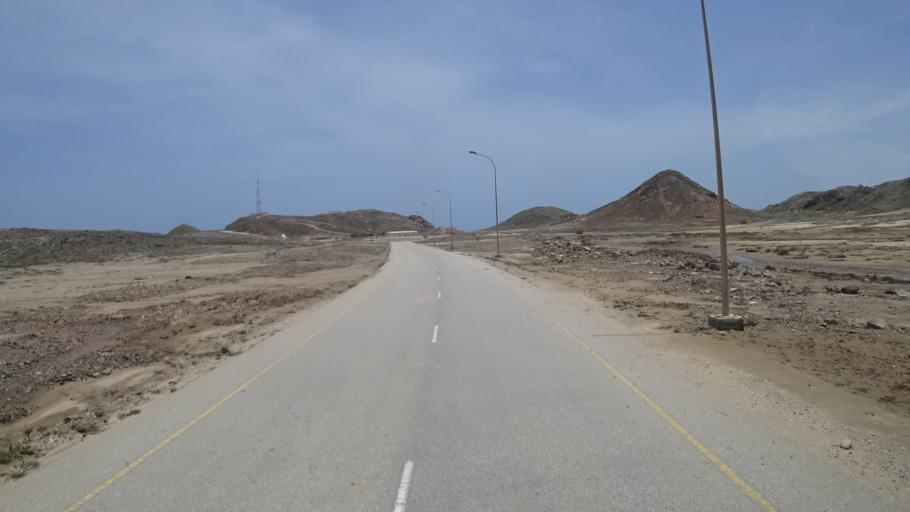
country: OM
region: Zufar
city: Salalah
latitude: 17.0077
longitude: 54.6949
